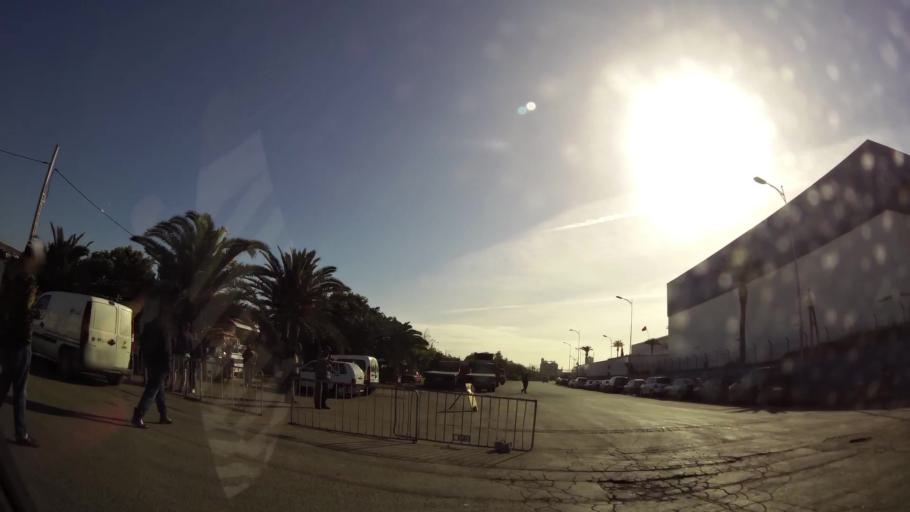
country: MA
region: Grand Casablanca
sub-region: Casablanca
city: Casablanca
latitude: 33.6043
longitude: -7.5746
